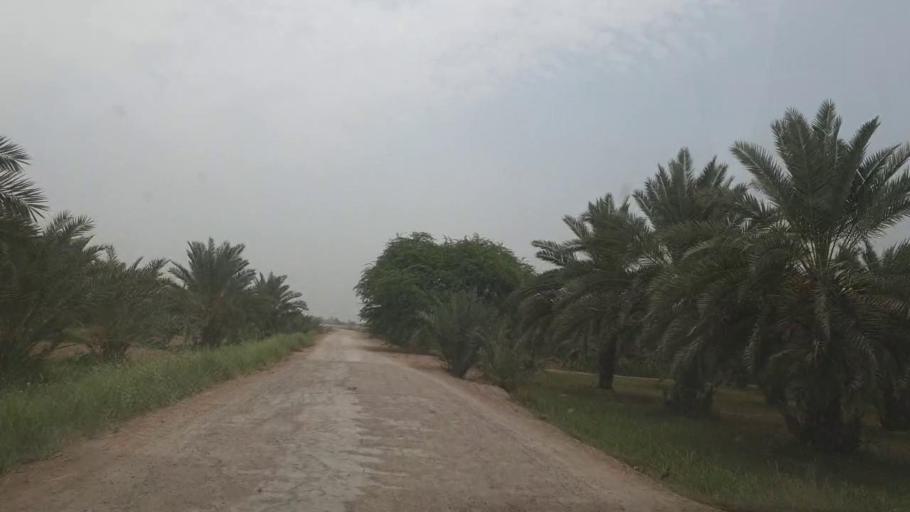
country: PK
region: Sindh
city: Kot Diji
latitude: 27.4328
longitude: 68.6284
